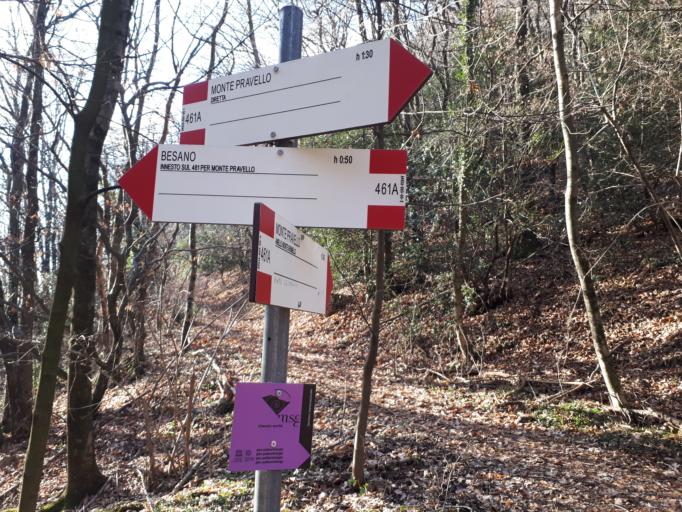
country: IT
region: Lombardy
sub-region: Provincia di Varese
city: Porto Ceresio
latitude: 45.8975
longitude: 8.9141
